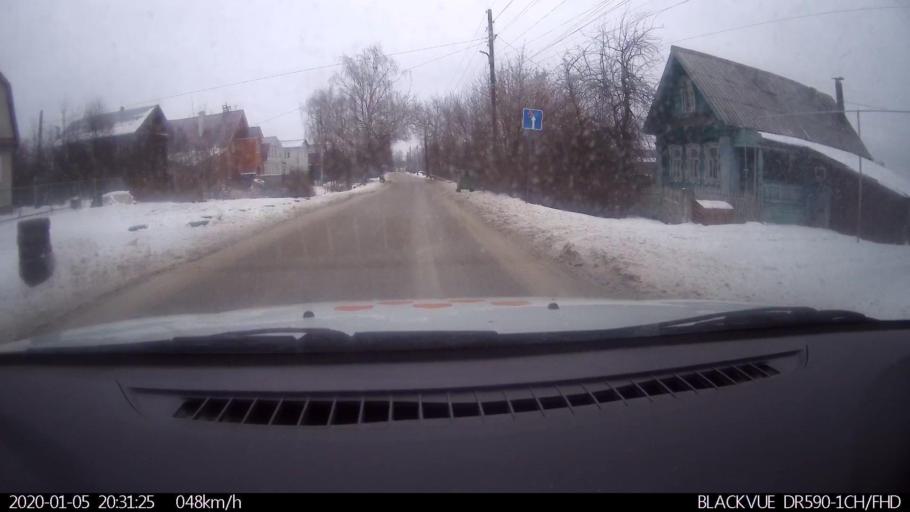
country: RU
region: Nizjnij Novgorod
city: Lukino
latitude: 56.4057
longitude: 43.7288
